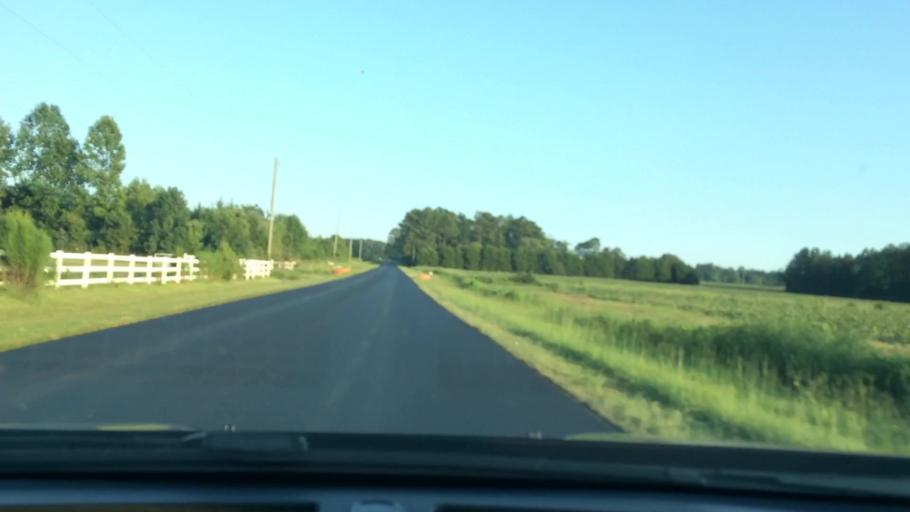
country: US
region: North Carolina
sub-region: Pitt County
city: Ayden
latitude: 35.4524
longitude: -77.4665
